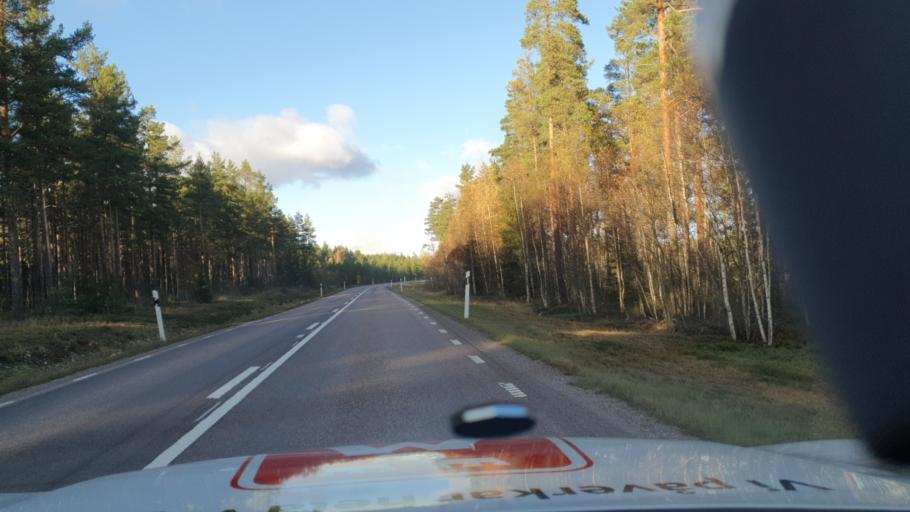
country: SE
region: Gaevleborg
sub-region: Gavle Kommun
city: Hedesunda
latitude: 60.5083
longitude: 16.9407
